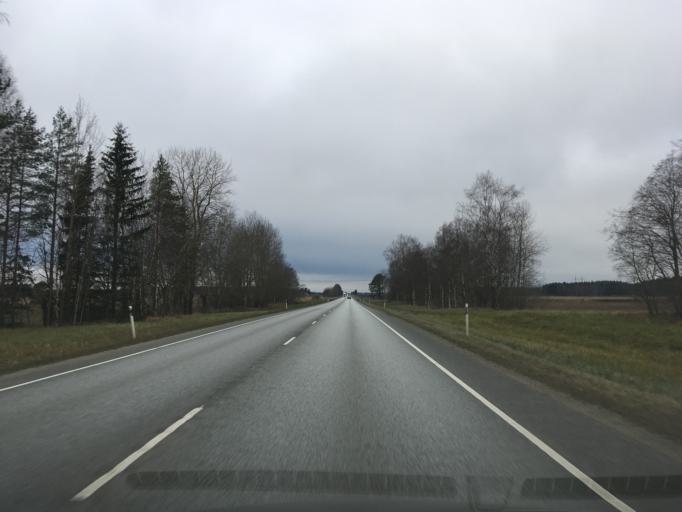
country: EE
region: Laeaene-Virumaa
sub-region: Someru vald
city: Someru
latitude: 59.3686
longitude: 26.5402
